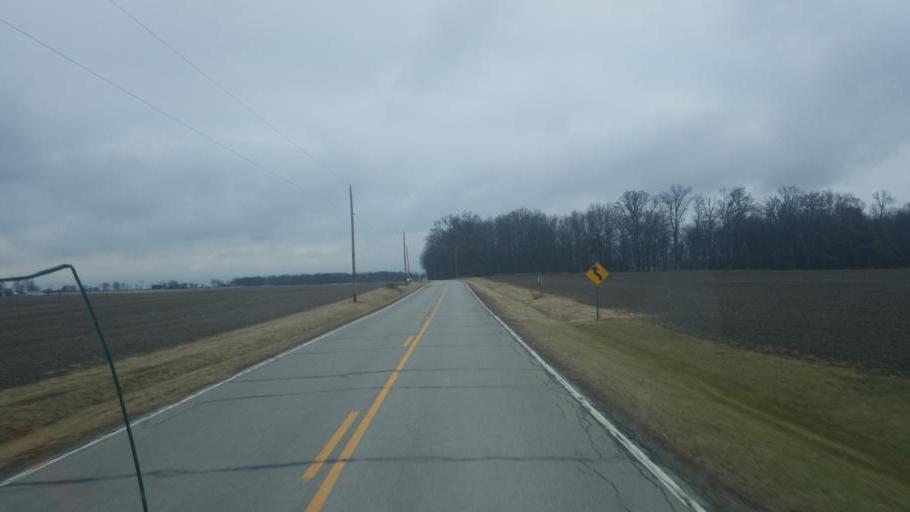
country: US
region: Ohio
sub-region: Crawford County
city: Bucyrus
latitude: 40.7306
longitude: -82.9530
